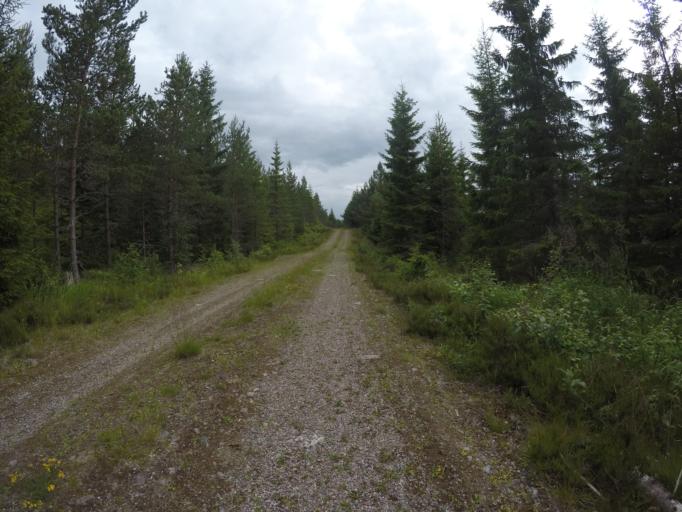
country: SE
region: Vaermland
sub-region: Filipstads Kommun
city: Lesjofors
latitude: 60.2144
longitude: 14.2629
